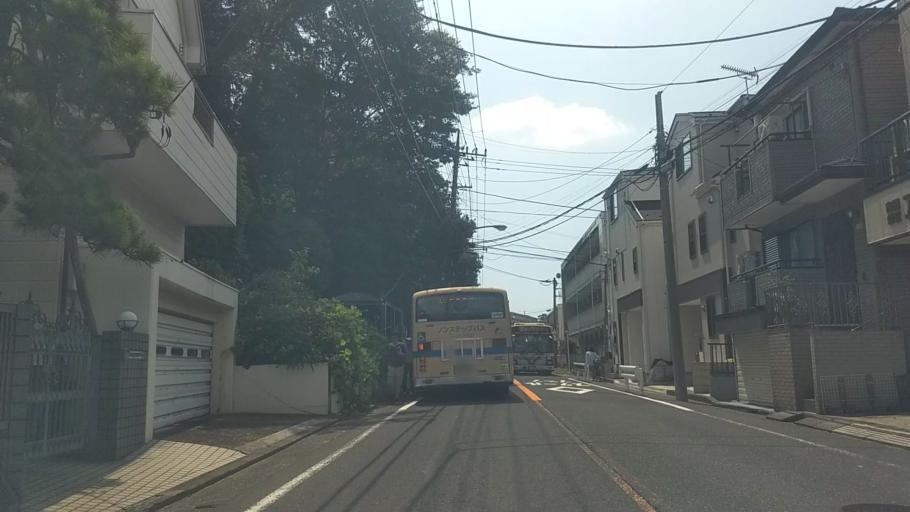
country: JP
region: Kanagawa
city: Yokohama
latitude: 35.5035
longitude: 139.6535
